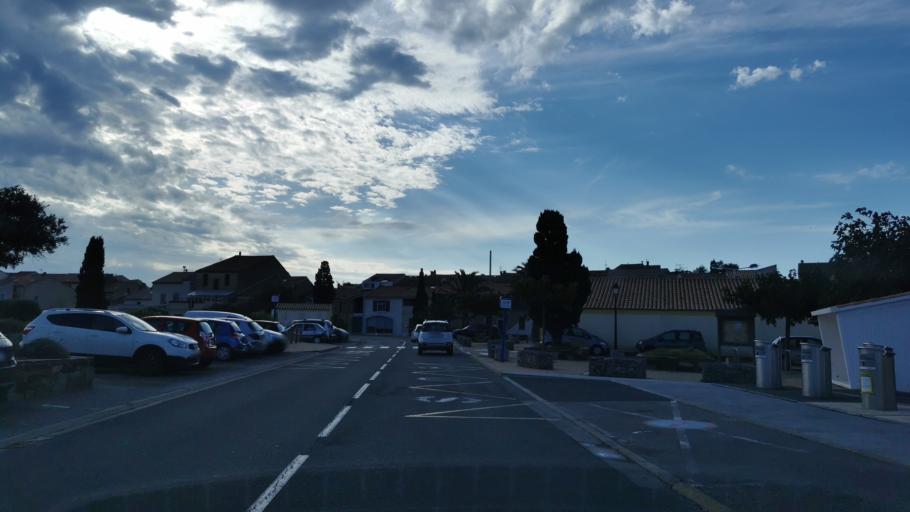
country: FR
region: Languedoc-Roussillon
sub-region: Departement de l'Aude
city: Gruissan
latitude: 43.1083
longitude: 3.0871
